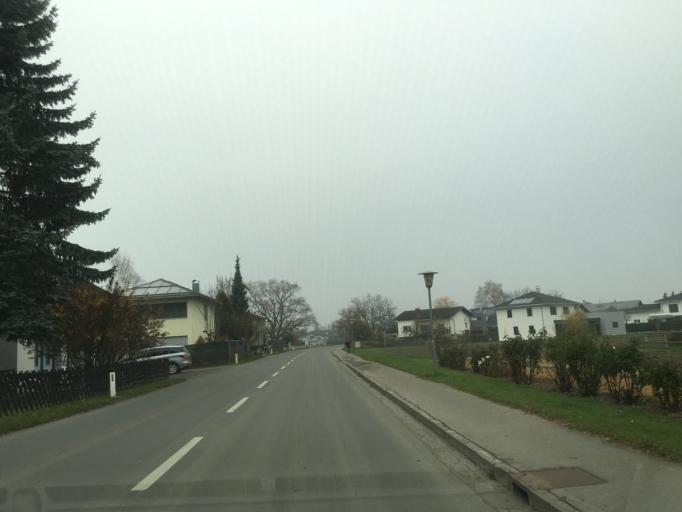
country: AT
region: Vorarlberg
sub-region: Politischer Bezirk Feldkirch
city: Koblach
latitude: 47.3185
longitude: 9.5985
